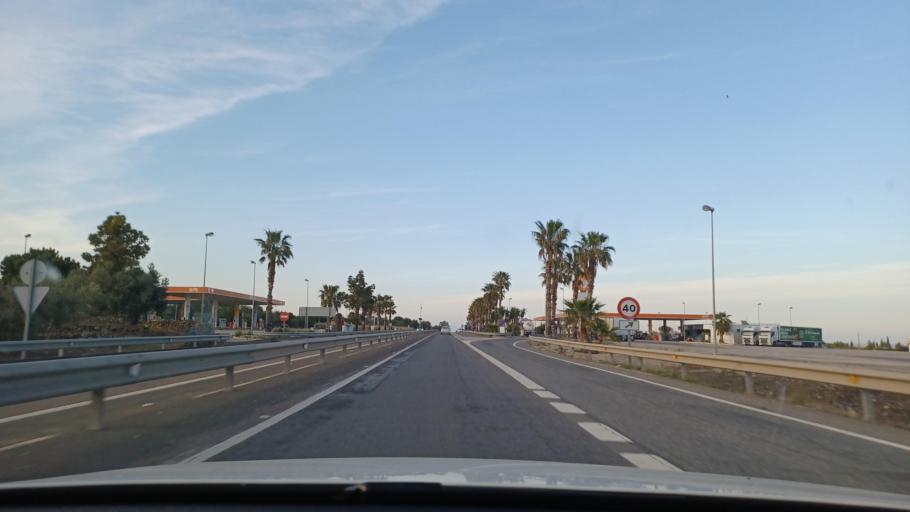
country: ES
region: Catalonia
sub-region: Provincia de Tarragona
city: Sant Carles de la Rapita
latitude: 40.6244
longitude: 0.5778
